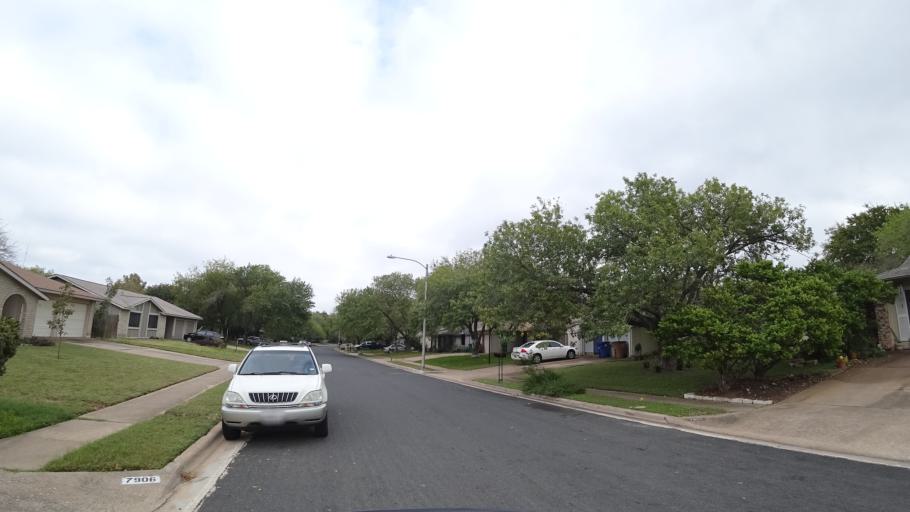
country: US
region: Texas
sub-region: Travis County
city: Shady Hollow
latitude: 30.2043
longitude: -97.8381
